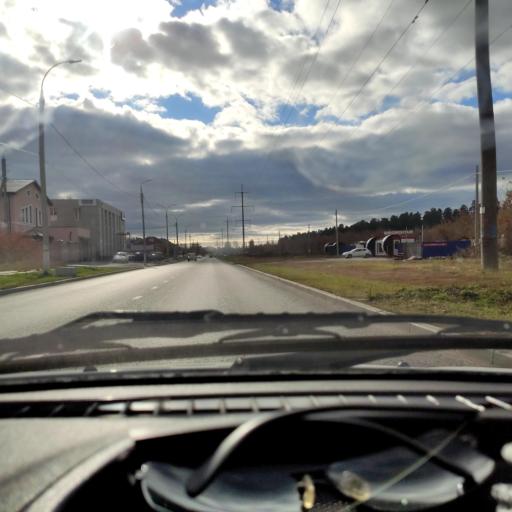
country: RU
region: Samara
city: Tol'yatti
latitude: 53.5209
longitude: 49.3957
